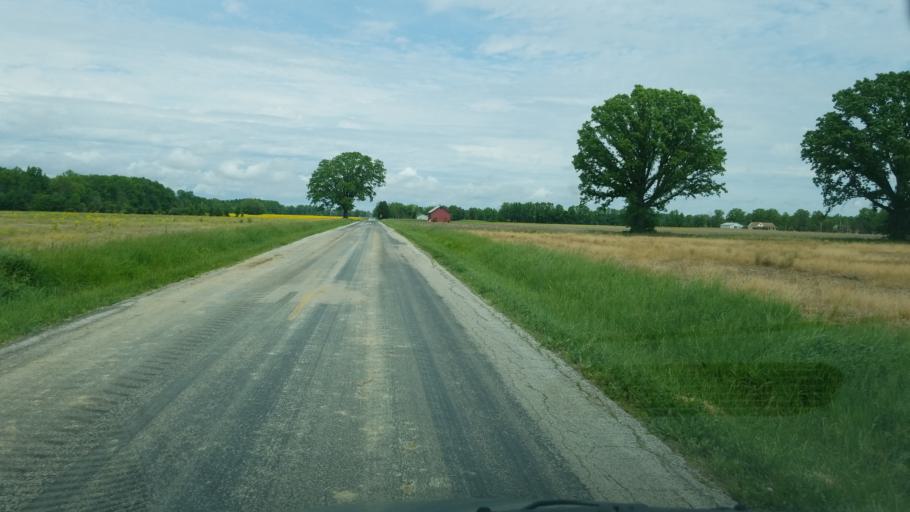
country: US
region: Ohio
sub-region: Morrow County
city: Cardington
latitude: 40.5387
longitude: -82.9767
